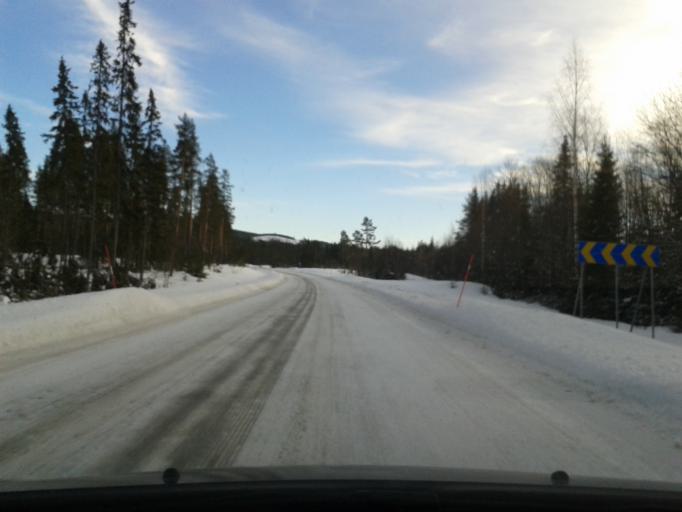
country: SE
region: Vaesterbotten
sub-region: Asele Kommun
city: Asele
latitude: 64.2783
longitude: 17.2679
